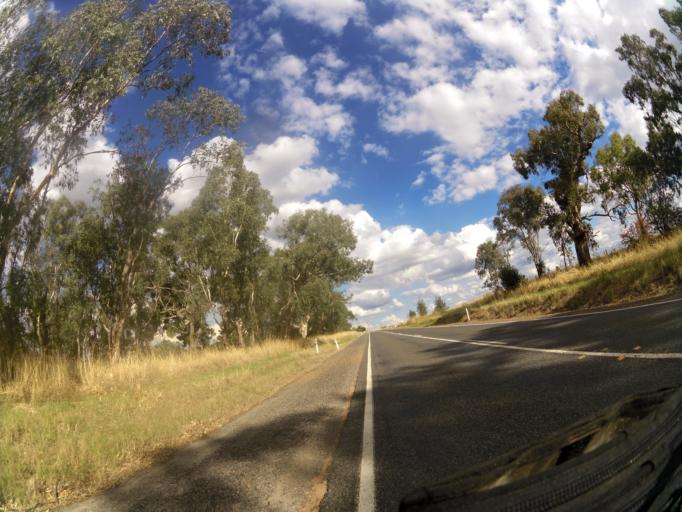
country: AU
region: Victoria
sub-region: Mansfield
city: Mansfield
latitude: -37.0199
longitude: 146.0925
